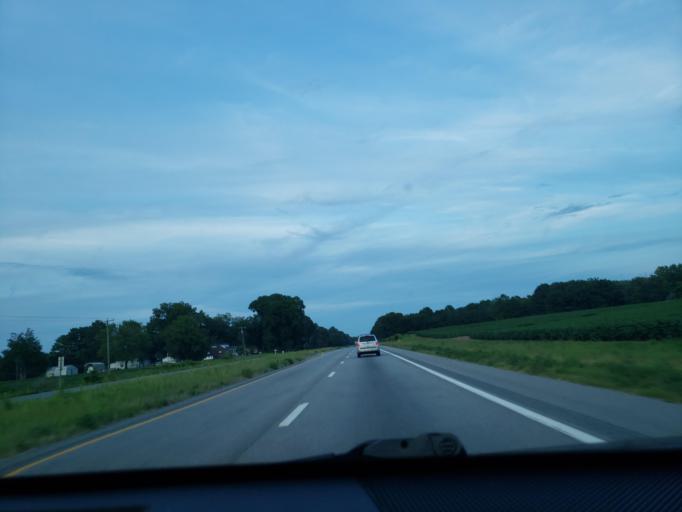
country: US
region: Virginia
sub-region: Southampton County
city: Courtland
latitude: 36.7044
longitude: -77.2160
